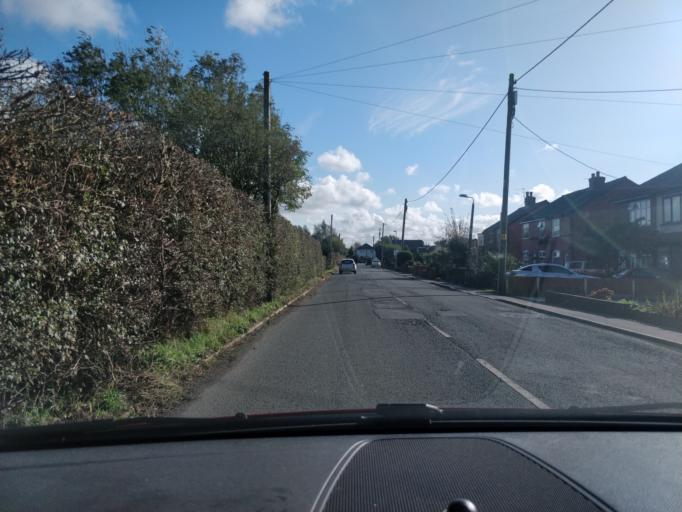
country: GB
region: England
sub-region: Lancashire
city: Banks
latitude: 53.6849
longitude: -2.9134
